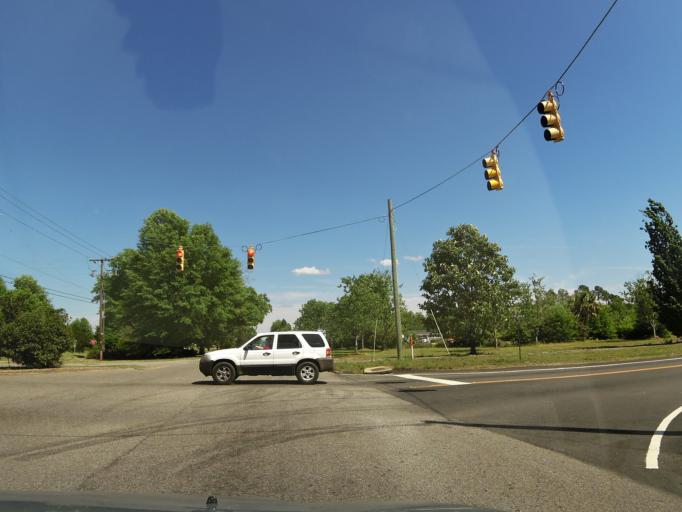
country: US
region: South Carolina
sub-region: Aiken County
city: Aiken
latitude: 33.5555
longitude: -81.7044
